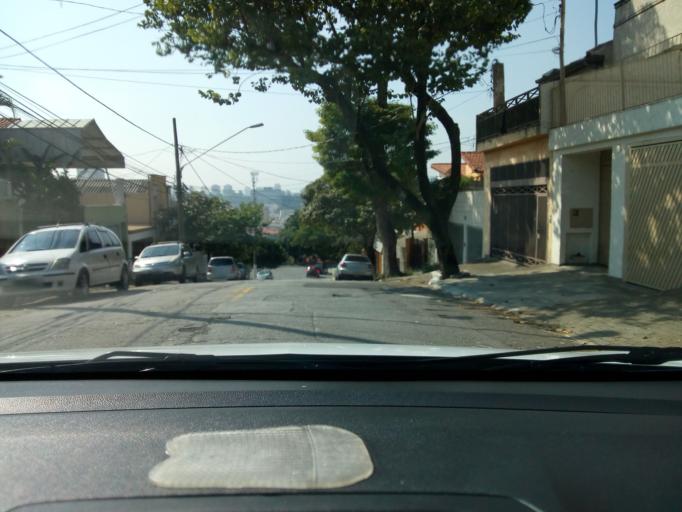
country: BR
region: Sao Paulo
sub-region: Sao Paulo
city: Sao Paulo
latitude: -23.5852
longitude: -46.6242
